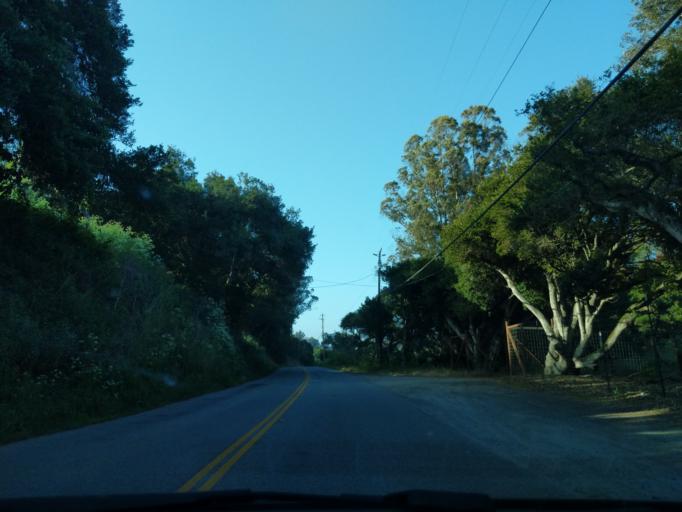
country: US
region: California
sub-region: Monterey County
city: Las Lomas
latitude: 36.8711
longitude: -121.6900
